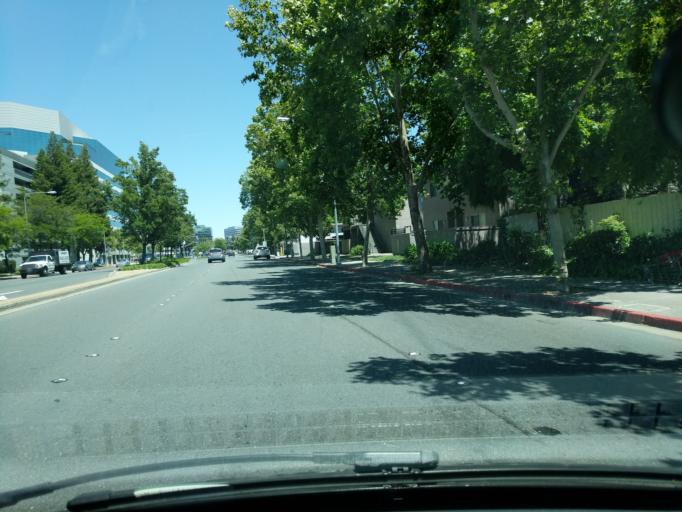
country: US
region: California
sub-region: Contra Costa County
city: Concord
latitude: 37.9700
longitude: -122.0448
